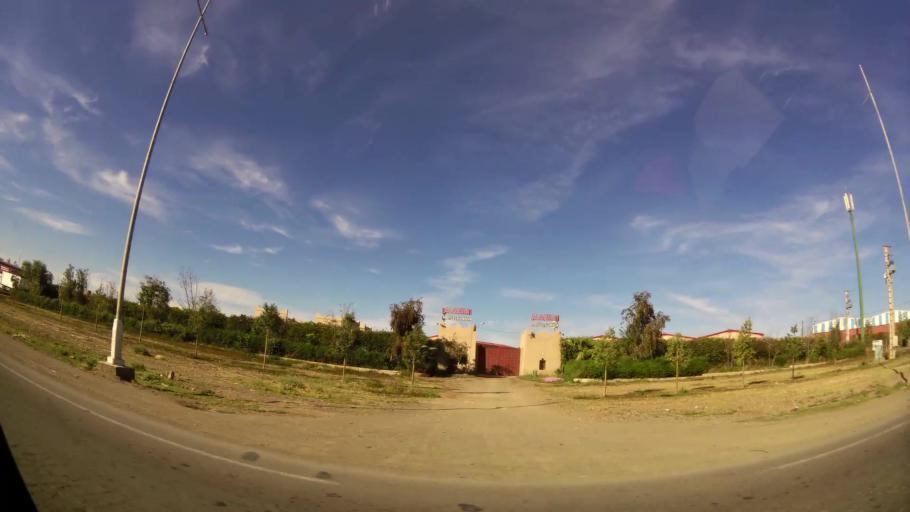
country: MA
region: Marrakech-Tensift-Al Haouz
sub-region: Marrakech
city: Marrakesh
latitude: 31.7111
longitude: -8.0694
